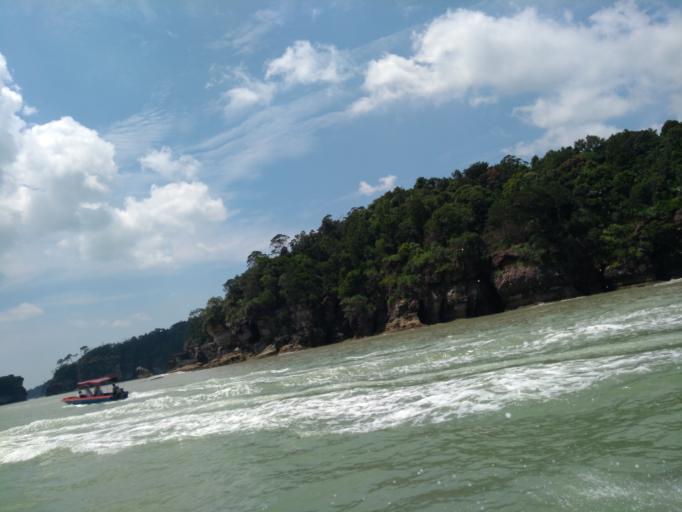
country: MY
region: Sarawak
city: Kuching
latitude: 1.7300
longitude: 110.4425
